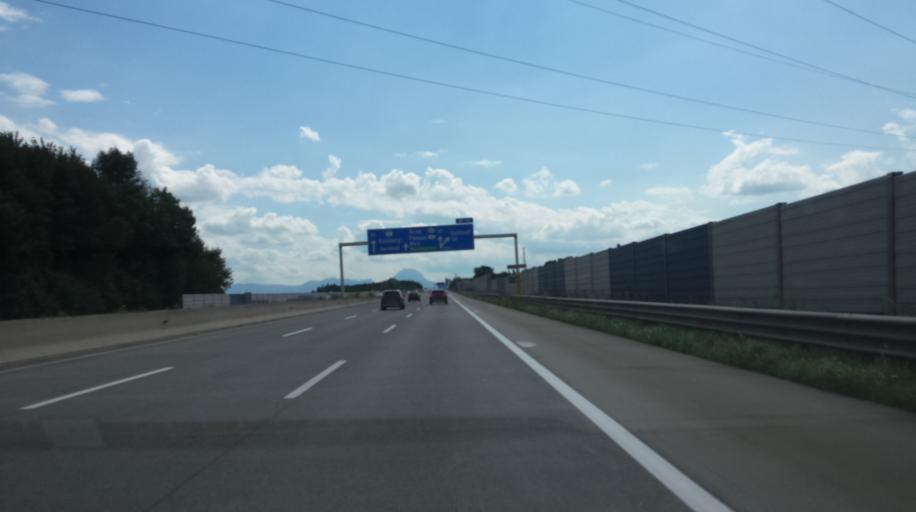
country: AT
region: Upper Austria
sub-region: Wels-Land
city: Sattledt
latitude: 48.0840
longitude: 14.0615
